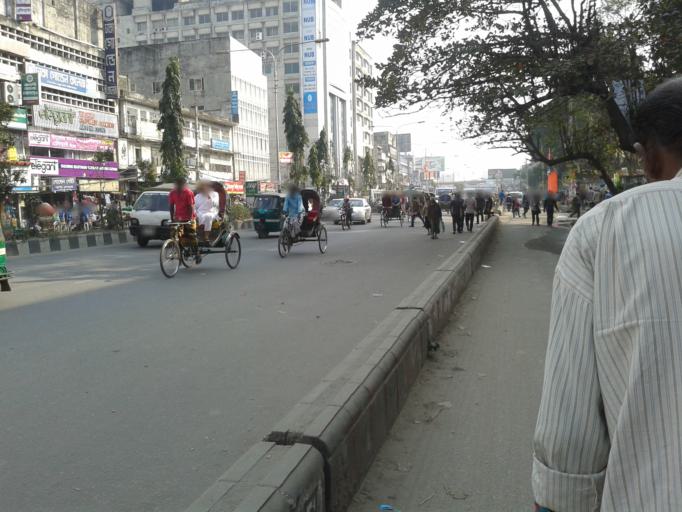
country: BD
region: Dhaka
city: Azimpur
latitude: 23.7371
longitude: 90.3837
